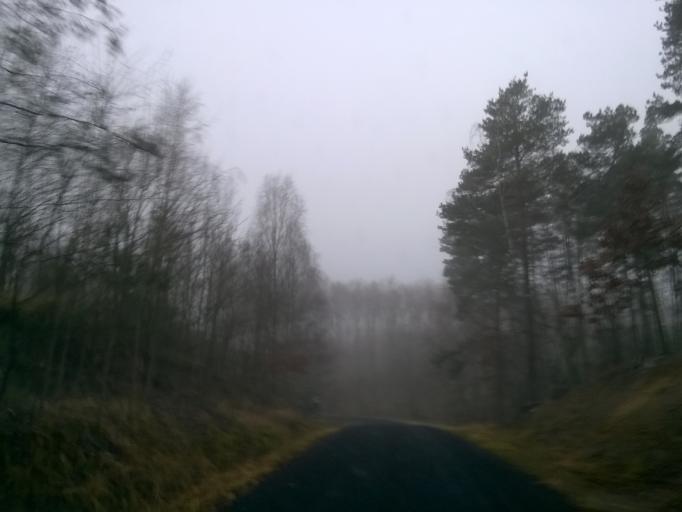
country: PL
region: Kujawsko-Pomorskie
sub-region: Powiat nakielski
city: Kcynia
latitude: 53.0471
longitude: 17.4922
